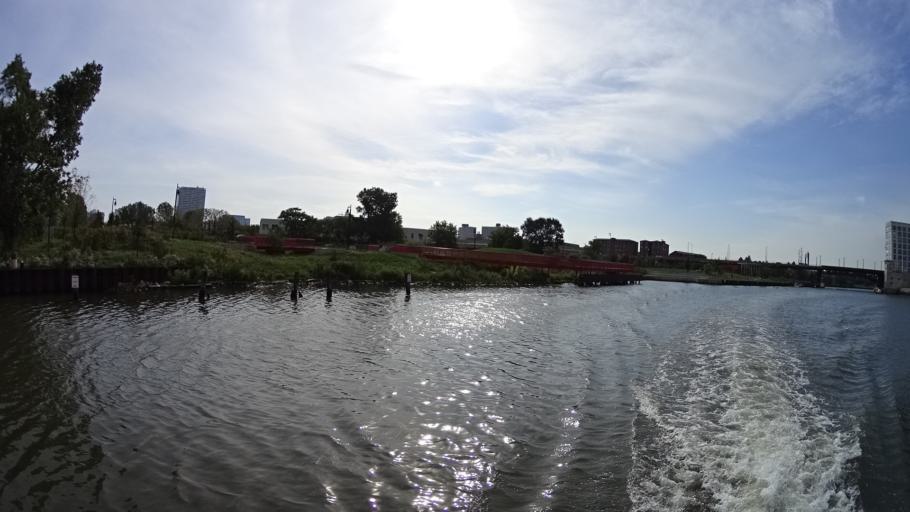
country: US
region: Illinois
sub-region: Cook County
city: Chicago
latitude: 41.8601
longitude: -87.6344
